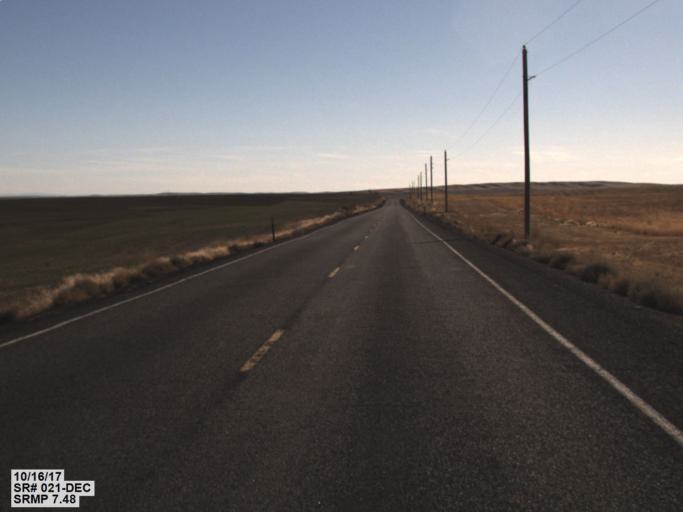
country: US
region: Washington
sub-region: Franklin County
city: Connell
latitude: 46.7345
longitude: -118.5478
